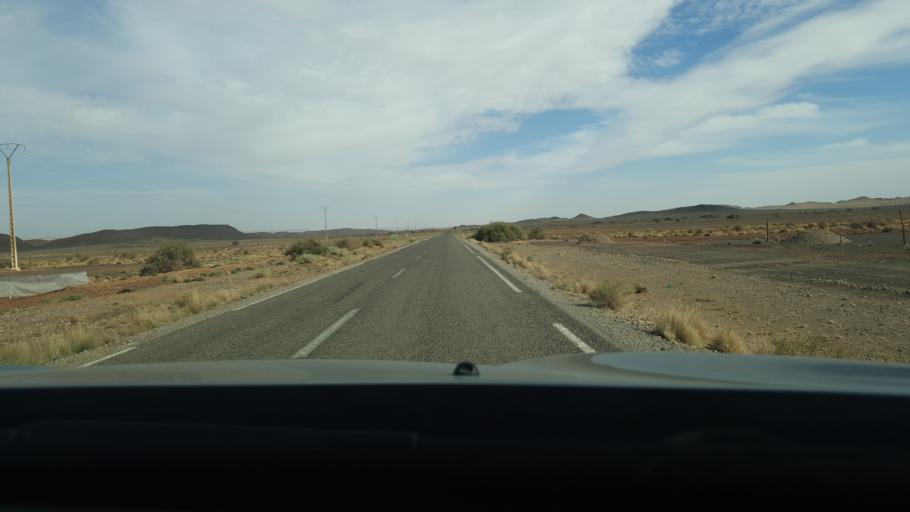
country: MA
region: Meknes-Tafilalet
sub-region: Errachidia
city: Goulmima
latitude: 31.5700
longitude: -4.8086
